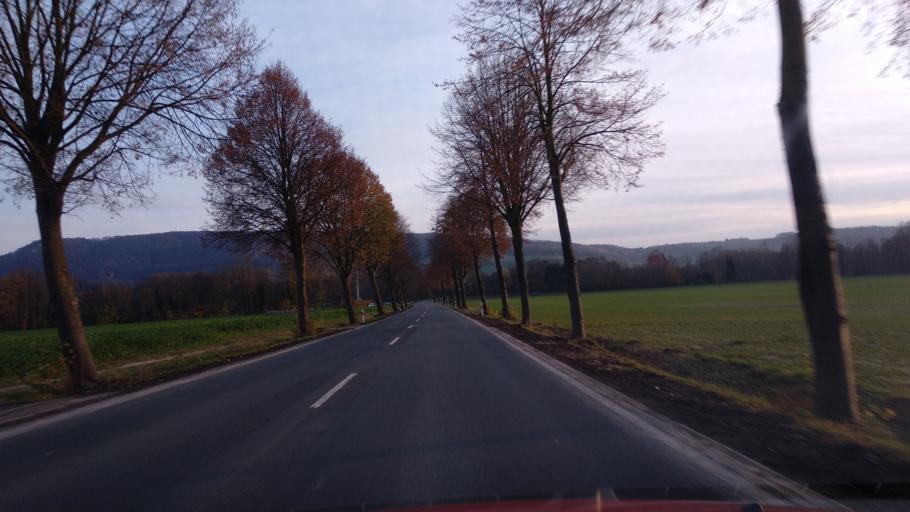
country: DE
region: Lower Saxony
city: Boffzen
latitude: 51.7191
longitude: 9.3407
